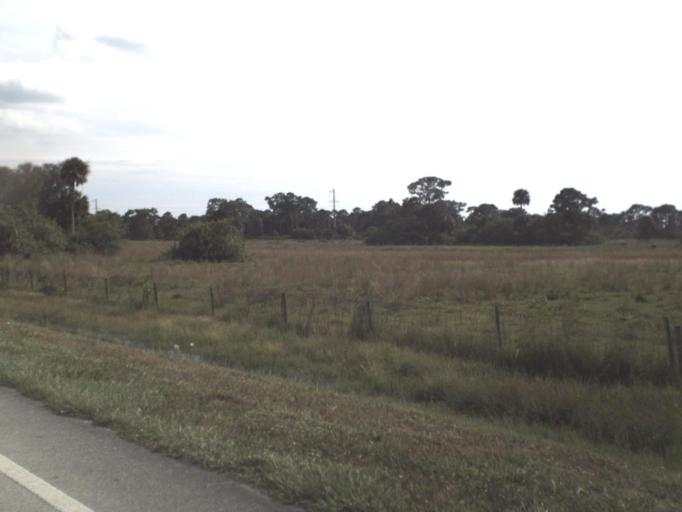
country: US
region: Florida
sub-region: Okeechobee County
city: Taylor Creek
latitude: 27.2237
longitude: -80.7675
